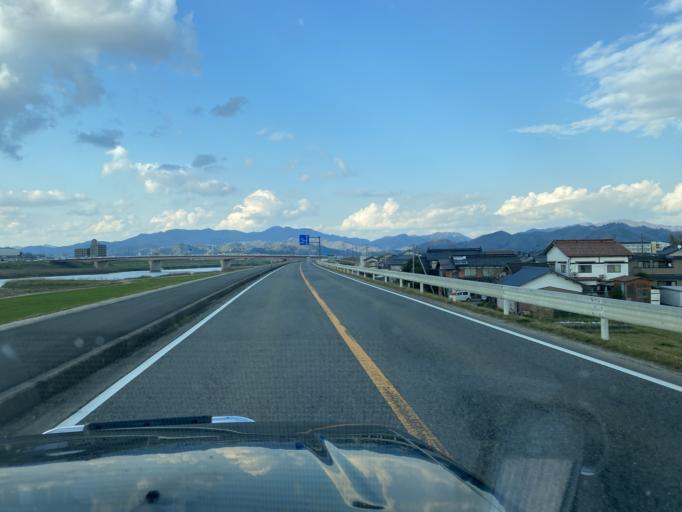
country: JP
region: Hyogo
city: Toyooka
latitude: 35.5220
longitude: 134.8253
